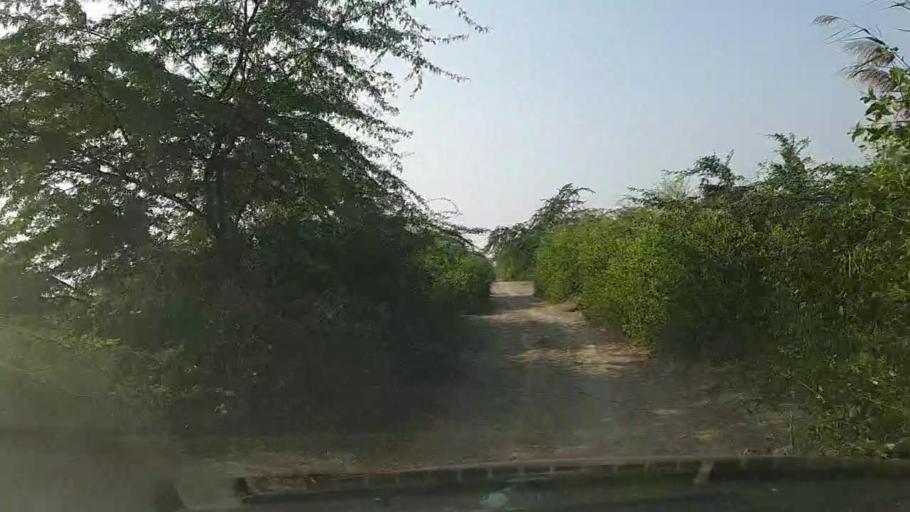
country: PK
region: Sindh
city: Mirpur Batoro
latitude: 24.6482
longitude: 68.2776
